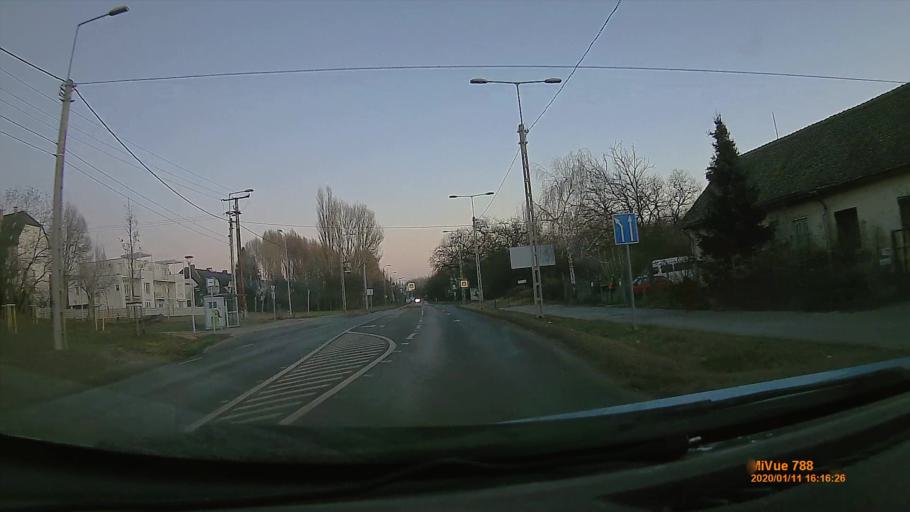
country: HU
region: Budapest
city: Budapest XVI. keruelet
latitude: 47.5265
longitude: 19.2009
